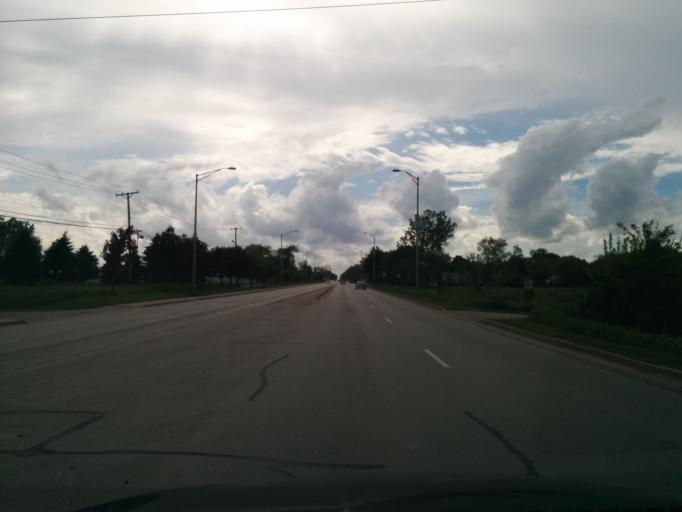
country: US
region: Illinois
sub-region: Will County
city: Romeoville
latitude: 41.6403
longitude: -88.0734
